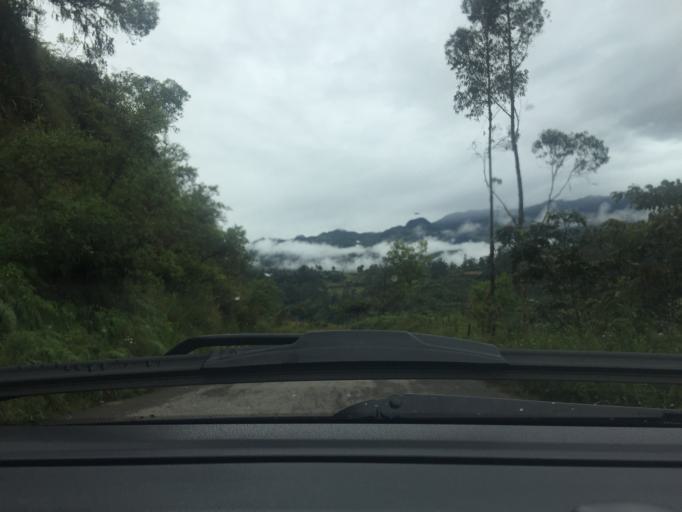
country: CO
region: Cundinamarca
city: Junin
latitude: 4.8102
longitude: -73.7071
